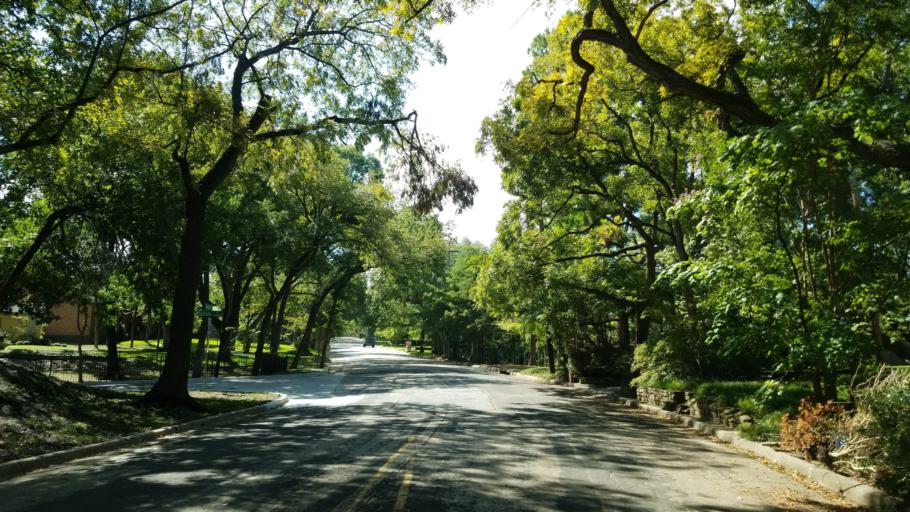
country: US
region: Texas
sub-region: Dallas County
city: Addison
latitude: 32.9369
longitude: -96.7980
